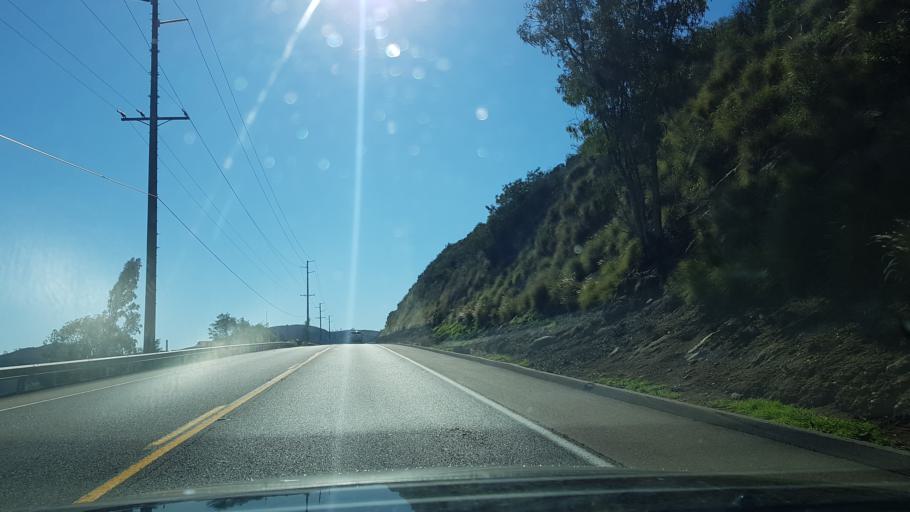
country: US
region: California
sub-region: San Diego County
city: Escondido
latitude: 33.0737
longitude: -117.1214
